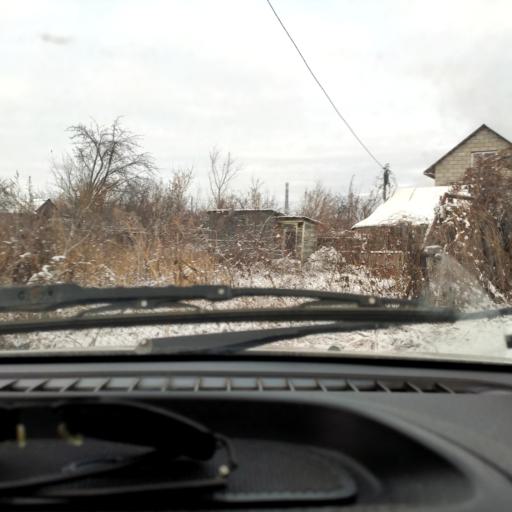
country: RU
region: Samara
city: Tol'yatti
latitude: 53.5428
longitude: 49.4320
